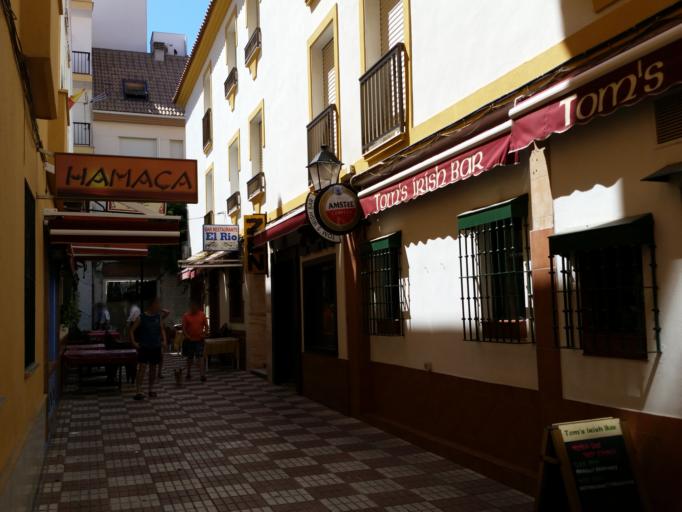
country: ES
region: Andalusia
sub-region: Provincia de Malaga
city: Fuengirola
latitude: 36.5528
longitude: -4.6142
